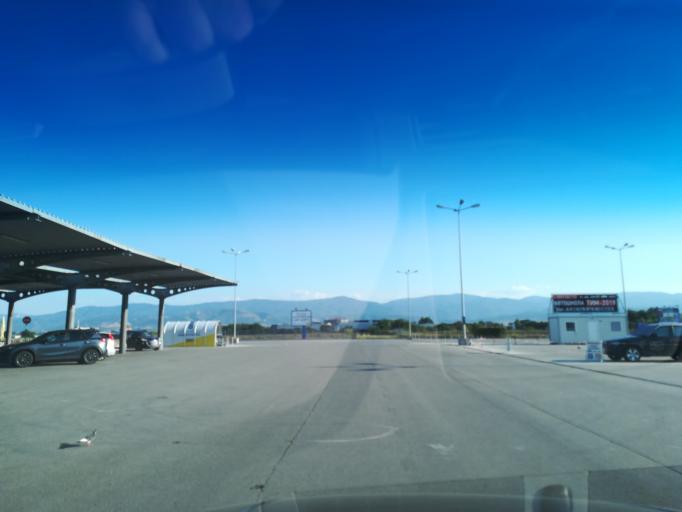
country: BG
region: Plovdiv
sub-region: Obshtina Plovdiv
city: Plovdiv
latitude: 42.1593
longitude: 24.6789
